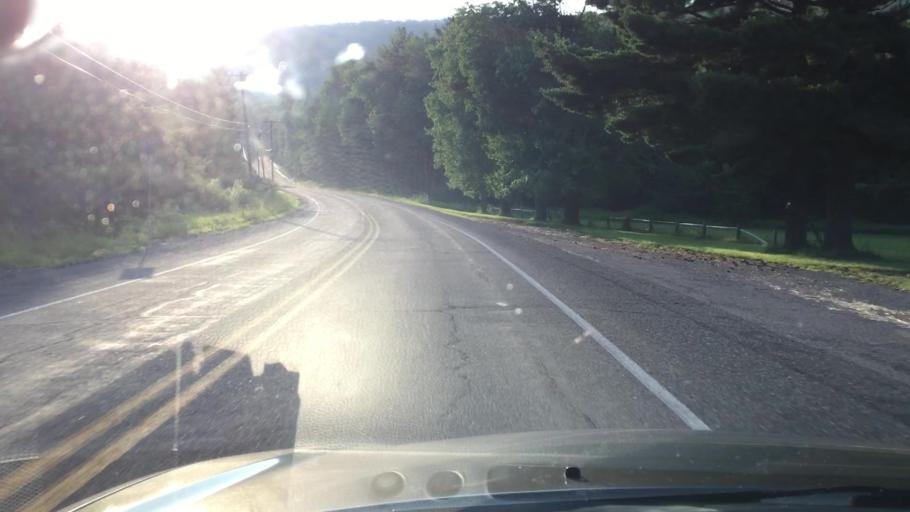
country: US
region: Pennsylvania
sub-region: Carbon County
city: Weatherly
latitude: 40.9257
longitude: -75.8676
